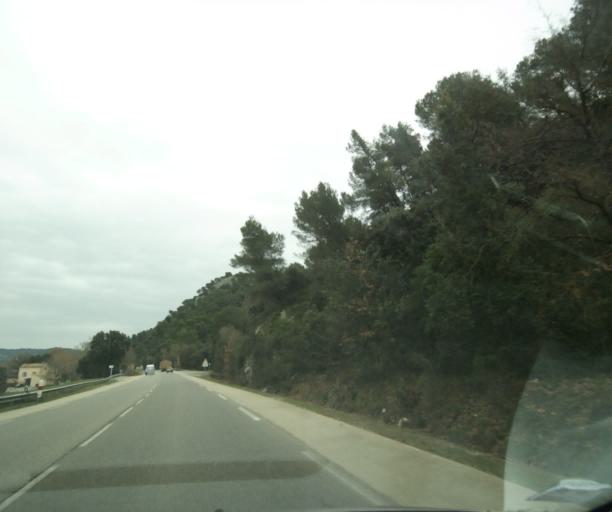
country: FR
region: Provence-Alpes-Cote d'Azur
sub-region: Departement des Bouches-du-Rhone
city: Jouques
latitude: 43.6584
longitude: 5.6328
